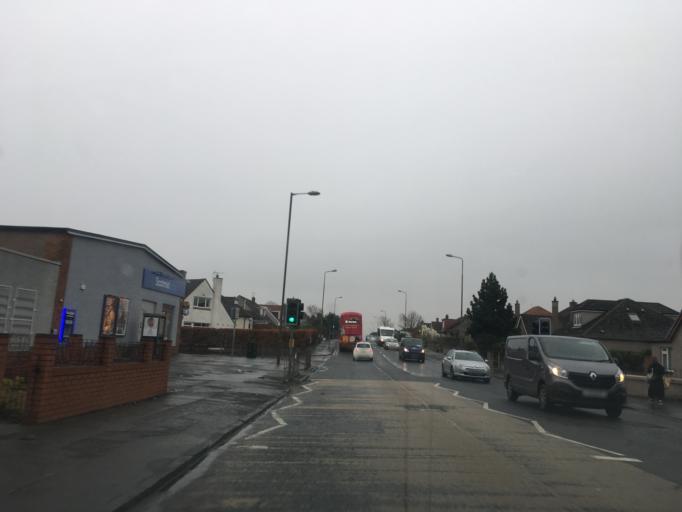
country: GB
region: Scotland
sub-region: Edinburgh
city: Currie
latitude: 55.9515
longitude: -3.2964
